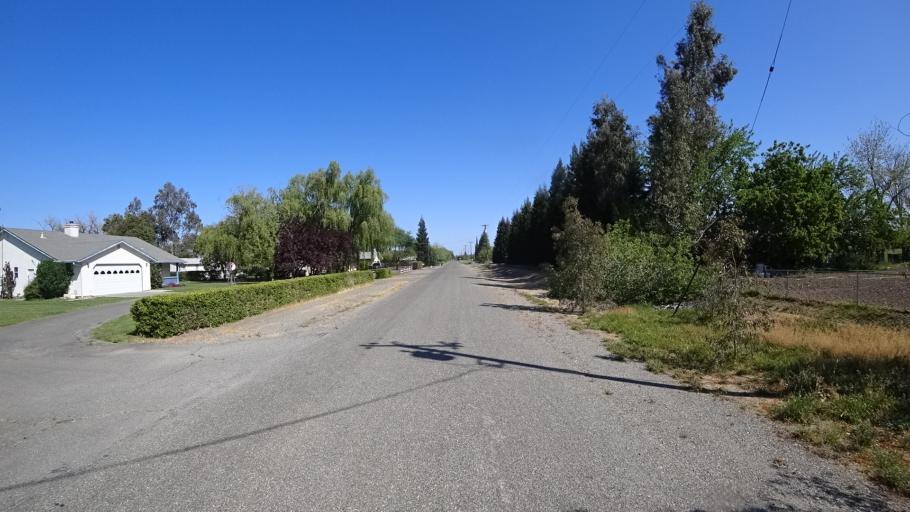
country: US
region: California
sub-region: Glenn County
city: Orland
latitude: 39.7218
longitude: -122.1925
